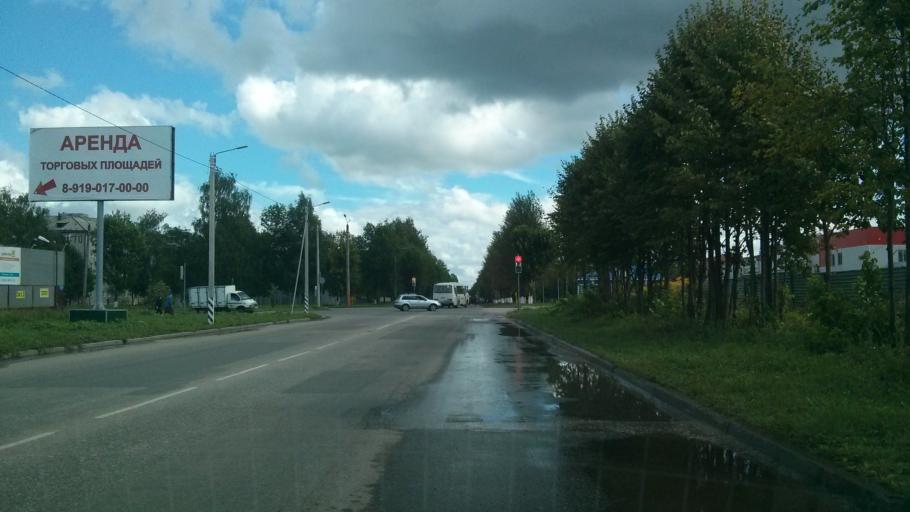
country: RU
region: Vladimir
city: Murom
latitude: 55.5471
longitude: 42.0633
